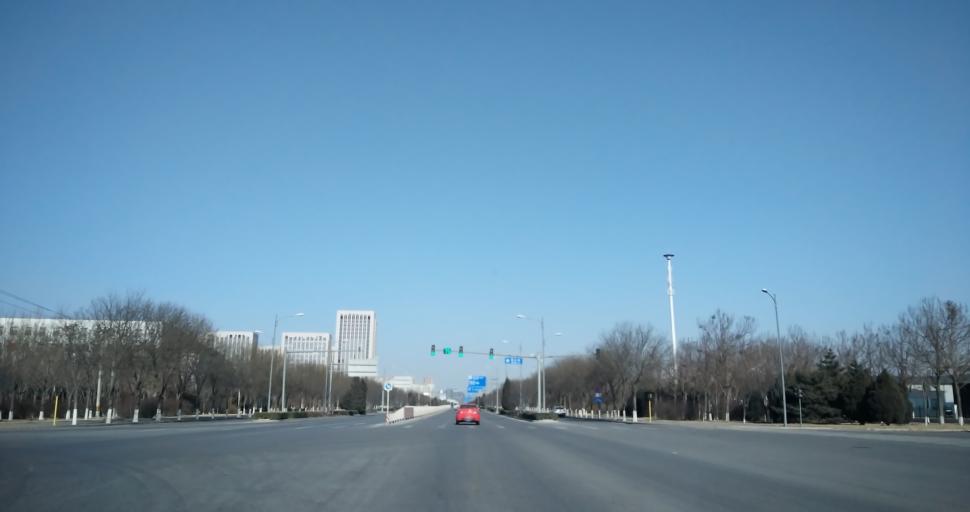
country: CN
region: Beijing
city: Yinghai
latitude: 39.7428
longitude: 116.4974
